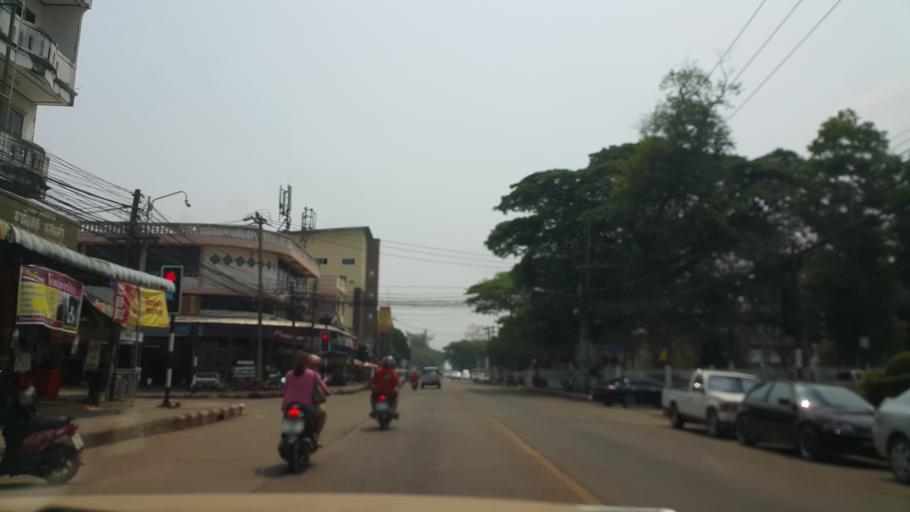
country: TH
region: Nakhon Phanom
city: Nakhon Phanom
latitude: 17.4110
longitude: 104.7796
